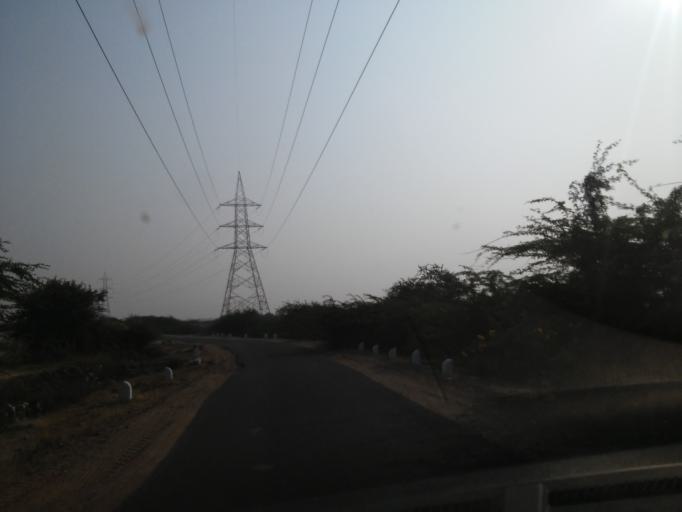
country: IN
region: Gujarat
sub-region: Kachchh
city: Mandvi
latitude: 22.8331
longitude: 69.5141
